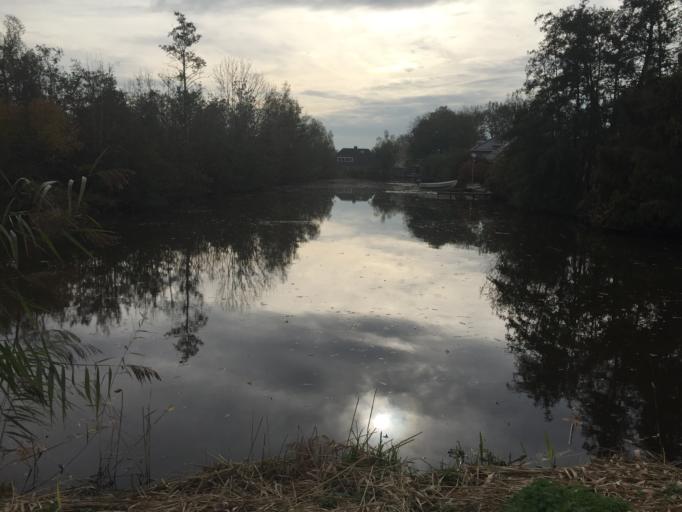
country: NL
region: Utrecht
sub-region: Gemeente De Ronde Venen
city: Mijdrecht
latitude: 52.1964
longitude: 4.8954
